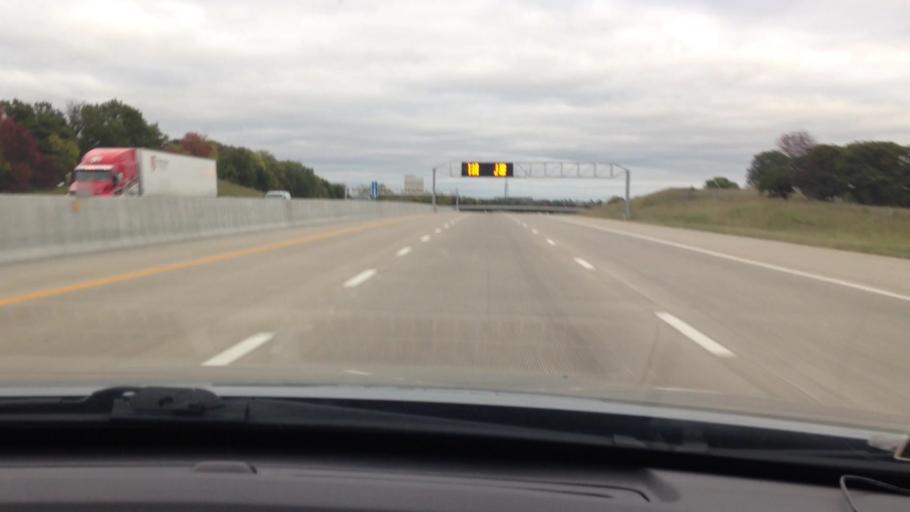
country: US
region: Kansas
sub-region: Wyandotte County
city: Bonner Springs
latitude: 39.1022
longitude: -94.8592
